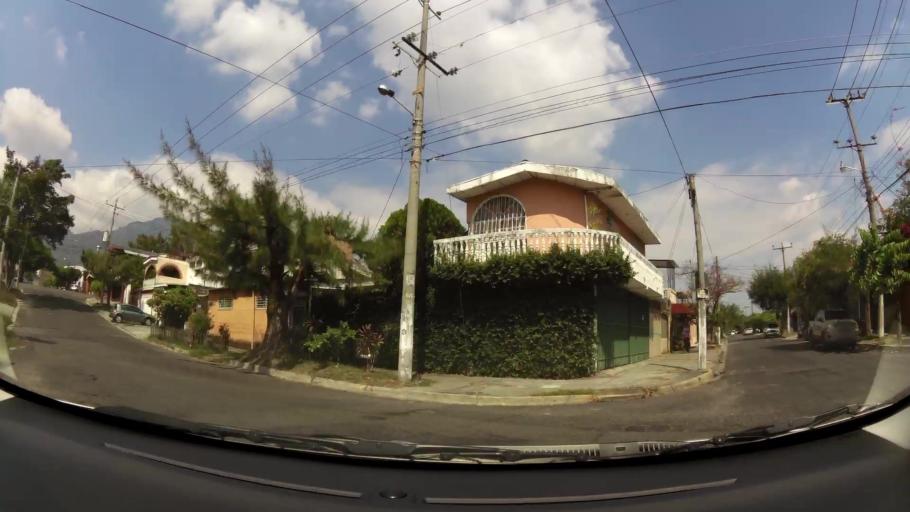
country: SV
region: San Salvador
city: Mejicanos
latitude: 13.7119
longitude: -89.2223
